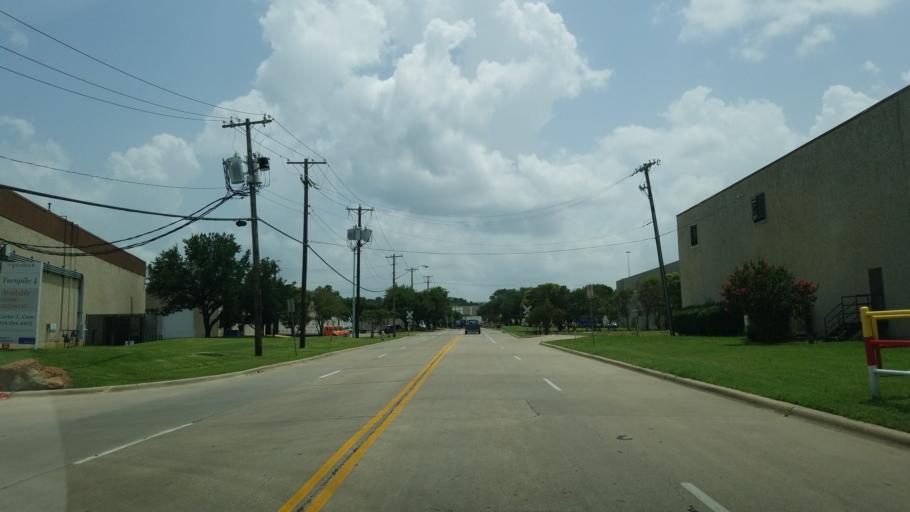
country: US
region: Texas
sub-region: Dallas County
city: Cockrell Hill
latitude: 32.7727
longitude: -96.8844
